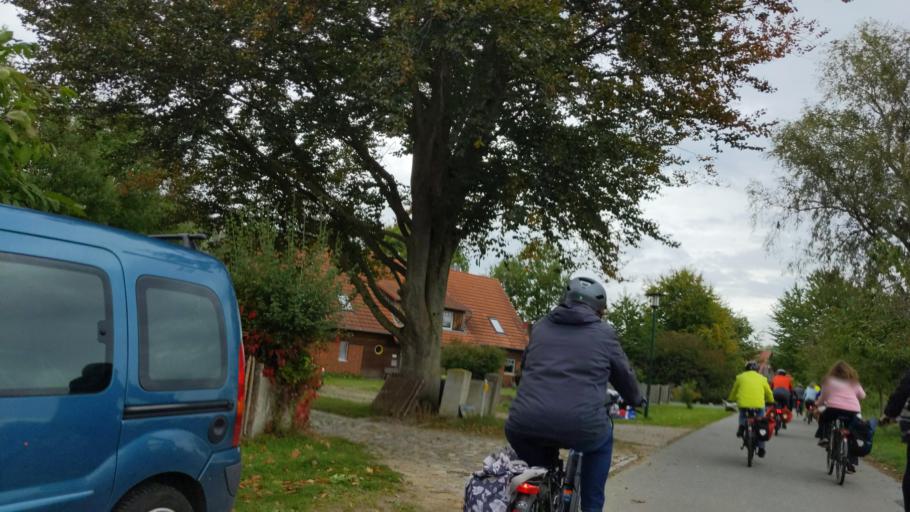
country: DE
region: Schleswig-Holstein
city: Gross Sarau
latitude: 53.7698
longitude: 10.7687
